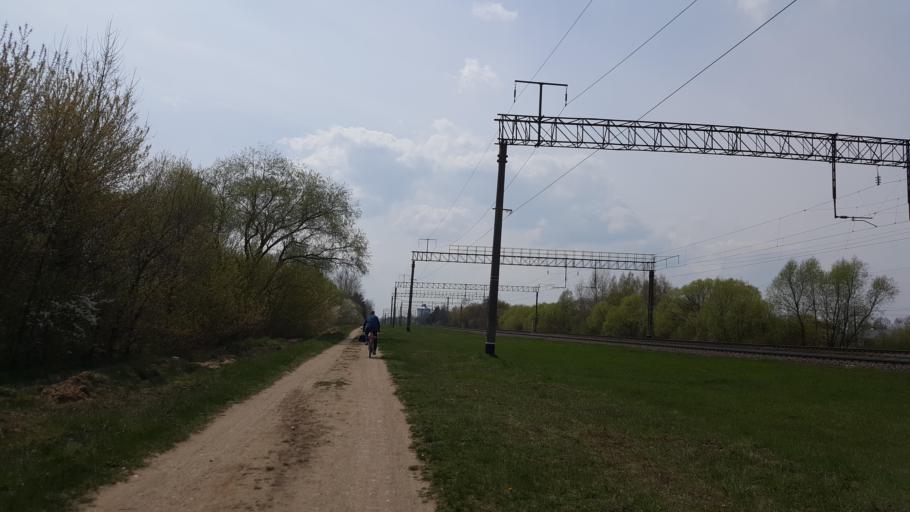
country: BY
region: Brest
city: Zhabinka
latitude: 52.1939
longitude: 23.9997
